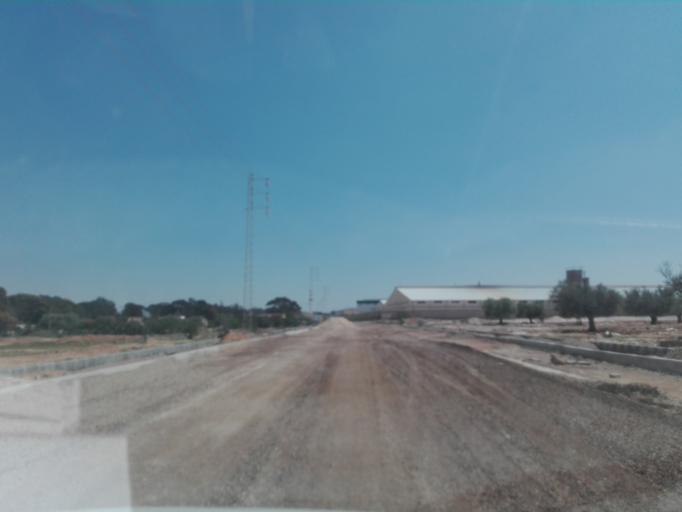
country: TN
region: Safaqis
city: Sfax
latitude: 34.7288
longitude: 10.5175
